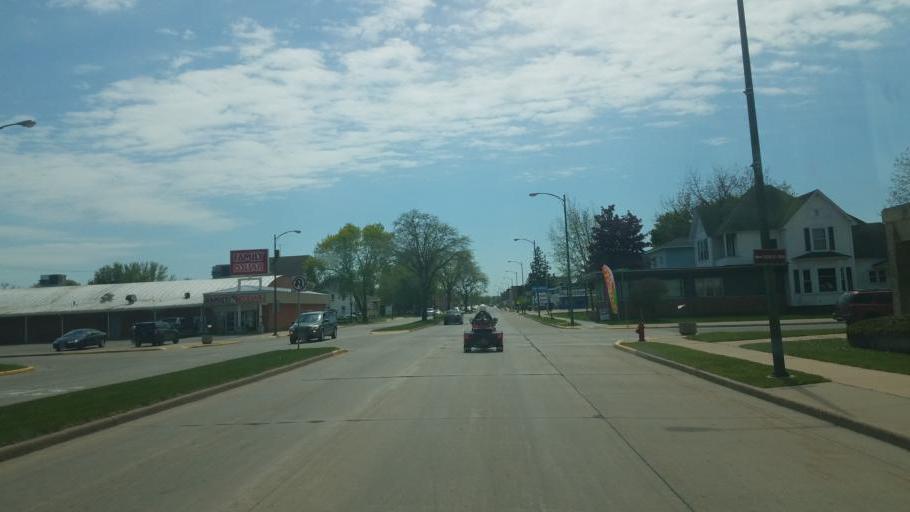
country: US
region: Wisconsin
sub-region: Monroe County
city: Tomah
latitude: 43.9819
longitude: -90.5048
